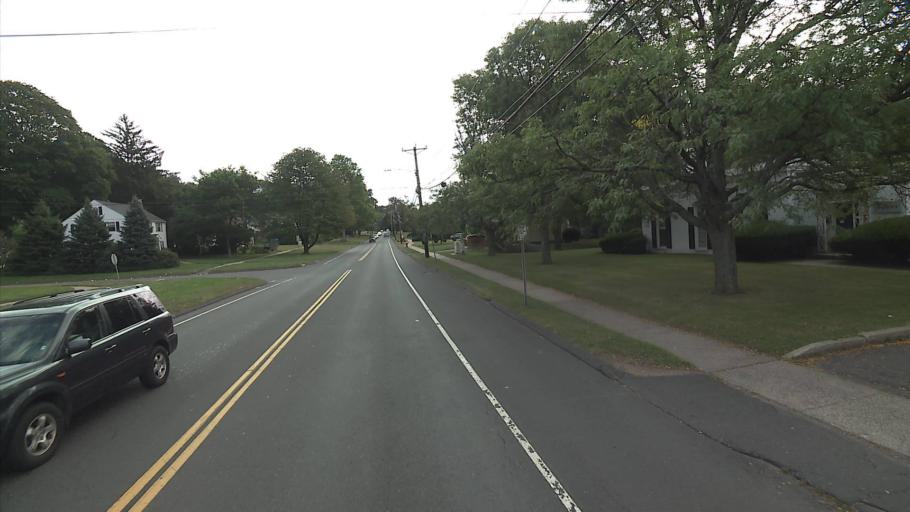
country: US
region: Connecticut
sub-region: Hartford County
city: Newington
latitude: 41.6903
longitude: -72.7218
